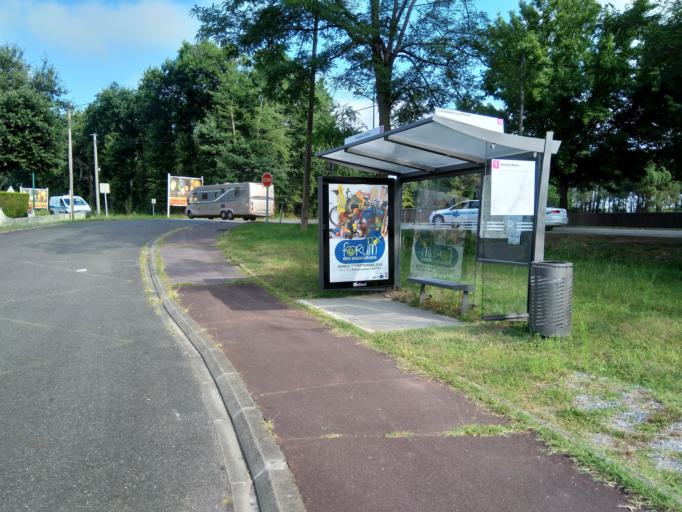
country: FR
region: Aquitaine
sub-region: Departement des Landes
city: Mees
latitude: 43.7299
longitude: -1.0932
